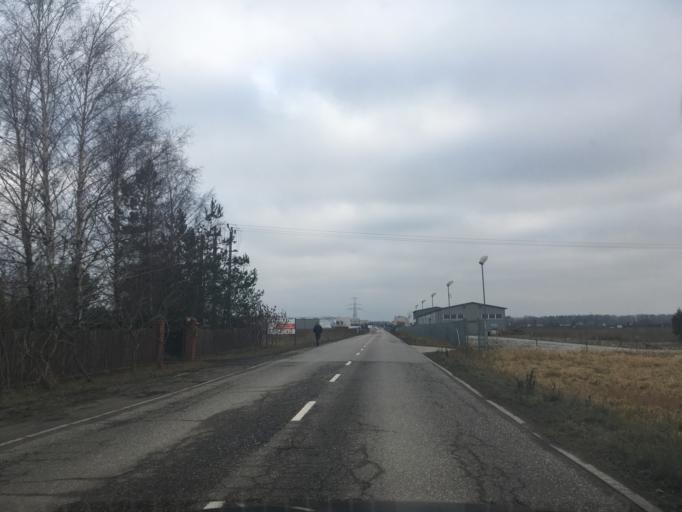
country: PL
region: Masovian Voivodeship
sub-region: Powiat piaseczynski
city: Lesznowola
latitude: 52.0874
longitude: 20.9699
